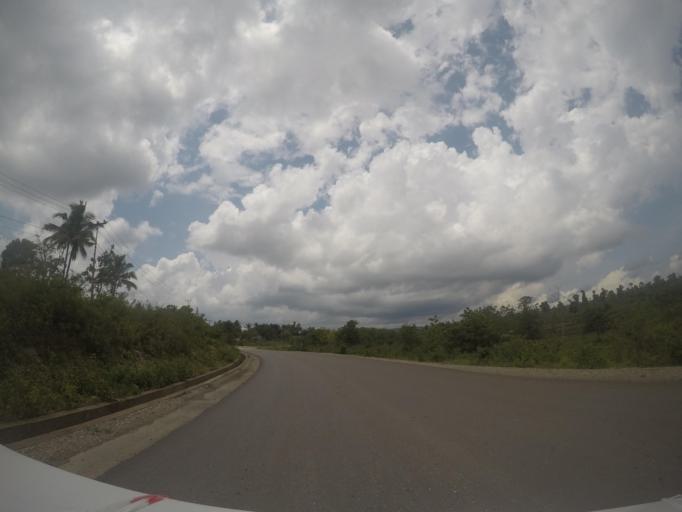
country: TL
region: Baucau
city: Venilale
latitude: -8.5595
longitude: 126.4016
